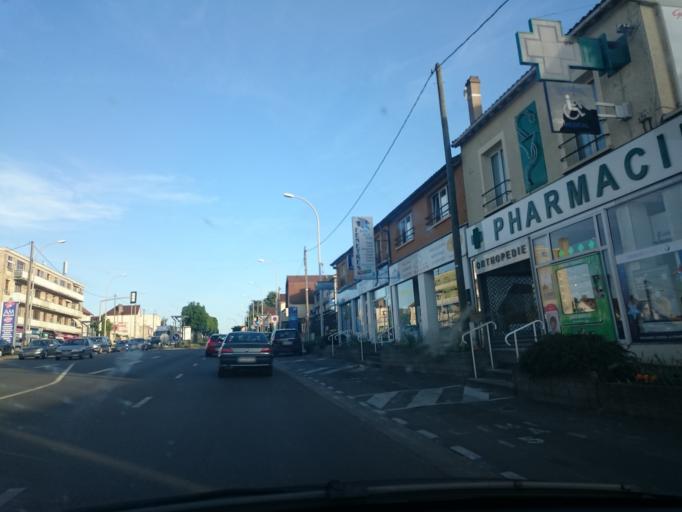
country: FR
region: Ile-de-France
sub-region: Departement de l'Essonne
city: Ris-Orangis
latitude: 48.6521
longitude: 2.4133
